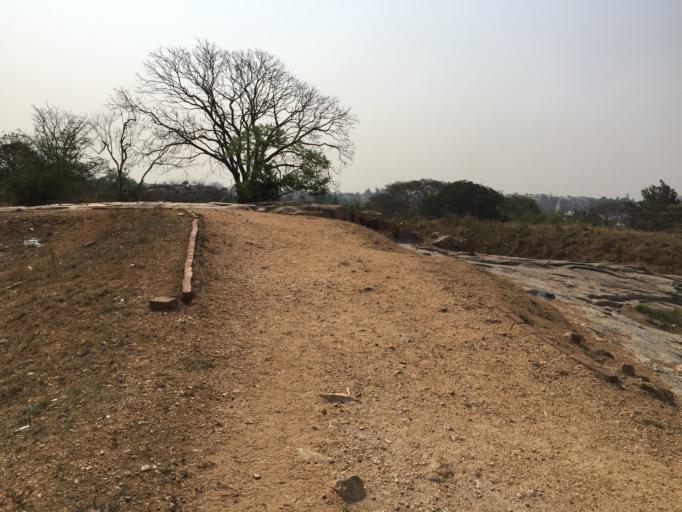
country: IN
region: Karnataka
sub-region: Bangalore Urban
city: Bangalore
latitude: 12.9483
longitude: 77.5899
